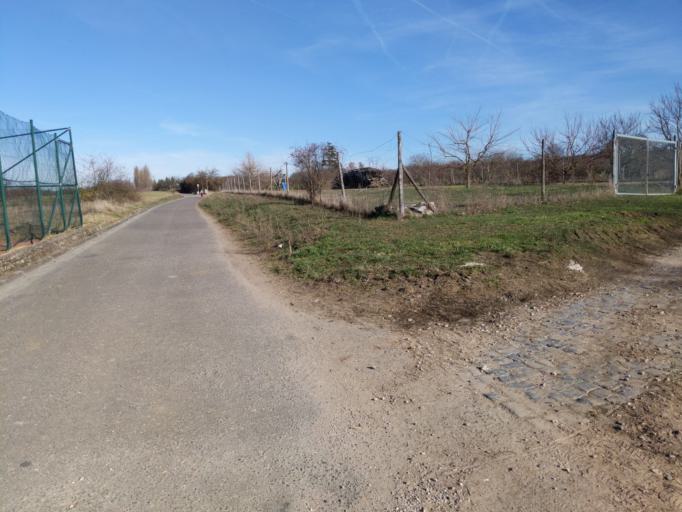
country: DE
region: Rheinland-Pfalz
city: Nieder-Ingelheim
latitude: 49.9813
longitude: 8.0794
